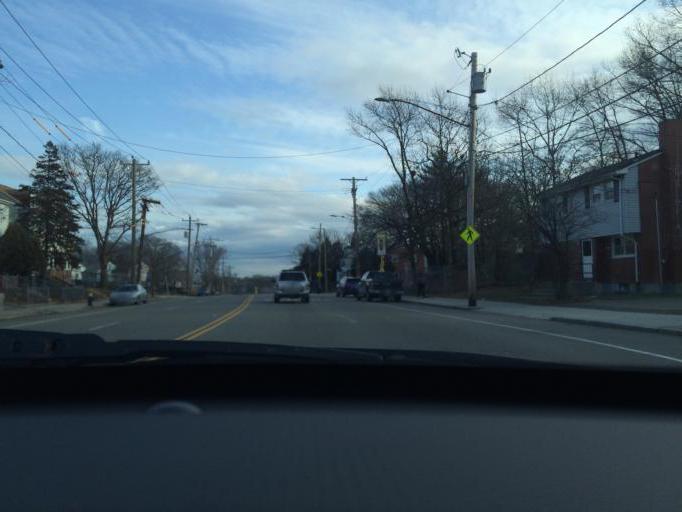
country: US
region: Massachusetts
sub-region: Norfolk County
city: Milton
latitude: 42.2782
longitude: -71.0792
